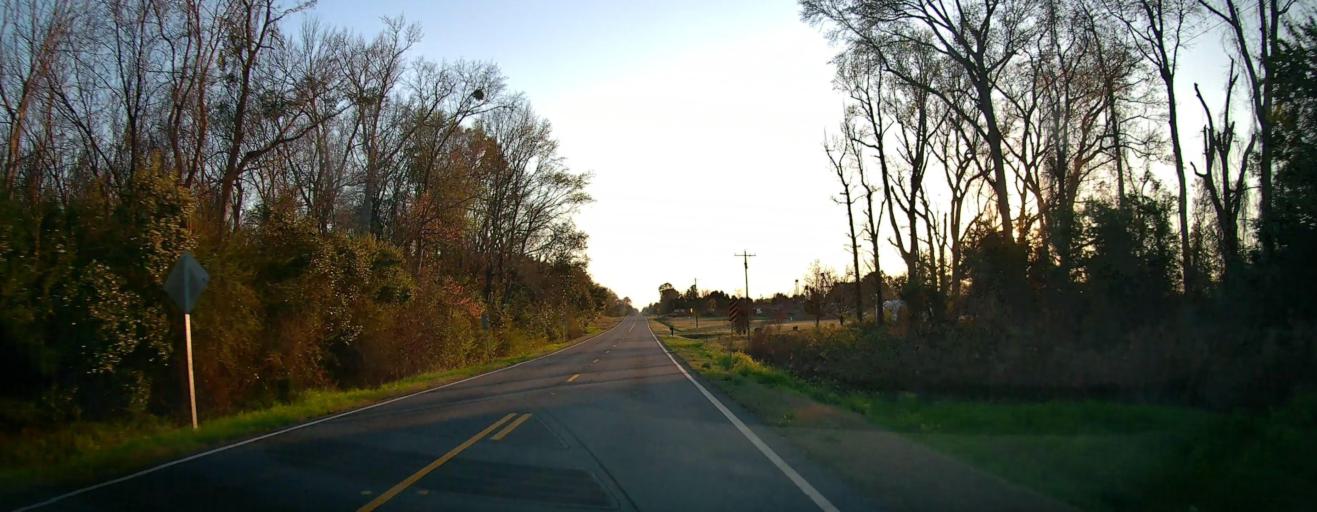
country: US
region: Georgia
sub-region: Dodge County
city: Chester
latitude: 32.3725
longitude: -82.9984
